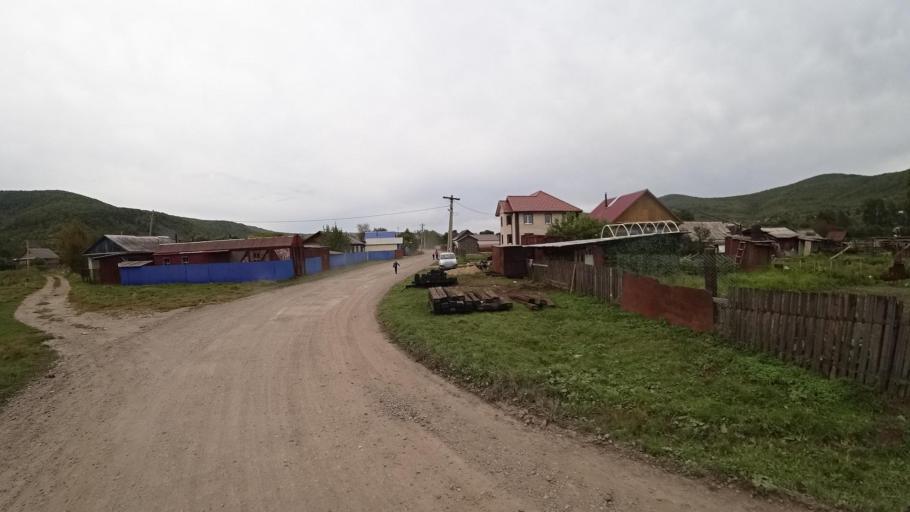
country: RU
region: Jewish Autonomous Oblast
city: Khingansk
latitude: 49.0314
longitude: 131.0490
